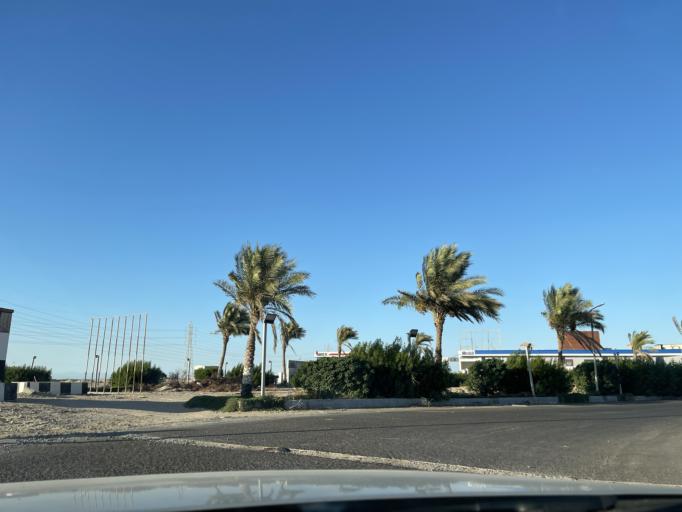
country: EG
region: Red Sea
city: Hurghada
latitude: 27.2328
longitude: 33.7805
